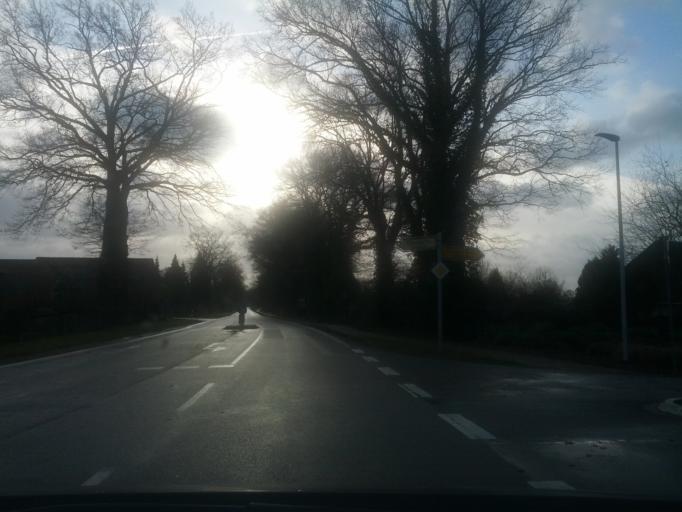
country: DE
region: Lower Saxony
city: Hamersen
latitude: 53.2534
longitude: 9.4816
